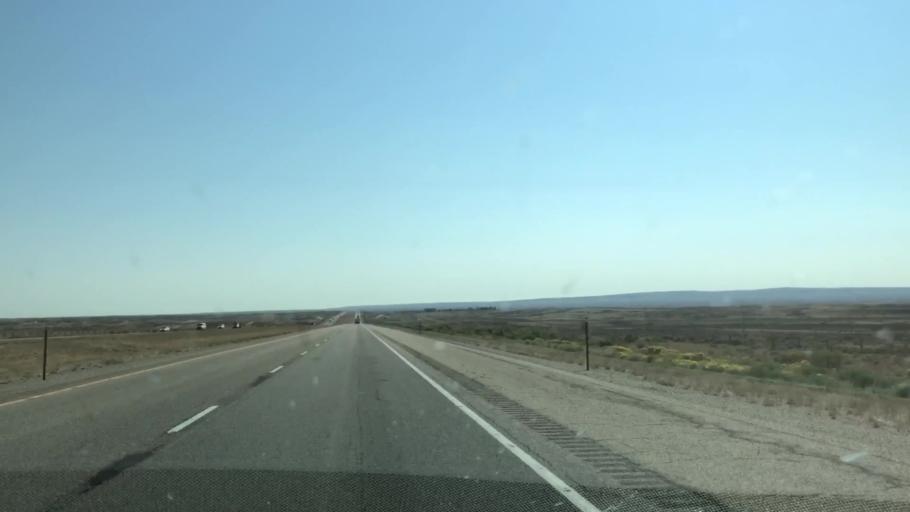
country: US
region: Wyoming
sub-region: Sweetwater County
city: Rock Springs
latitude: 41.6412
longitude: -108.5107
